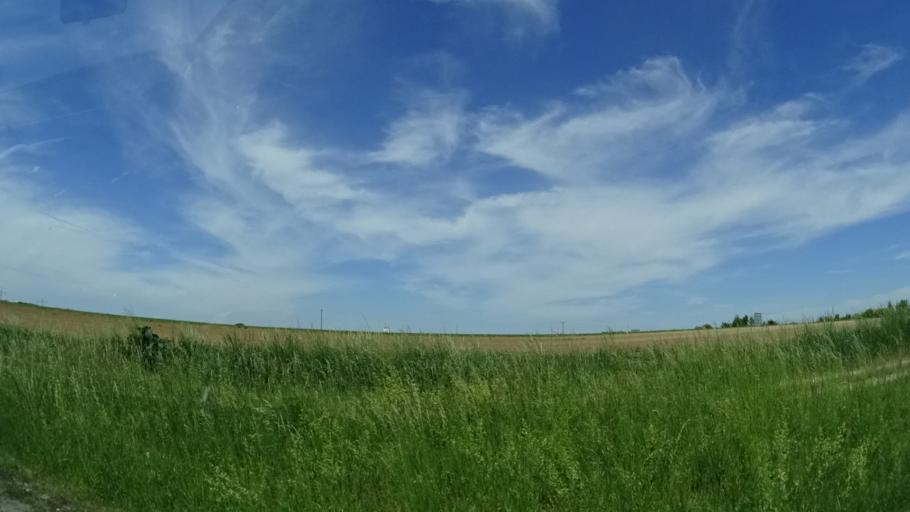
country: DE
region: Bavaria
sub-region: Regierungsbezirk Unterfranken
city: Euerbach
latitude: 50.0607
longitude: 10.1476
